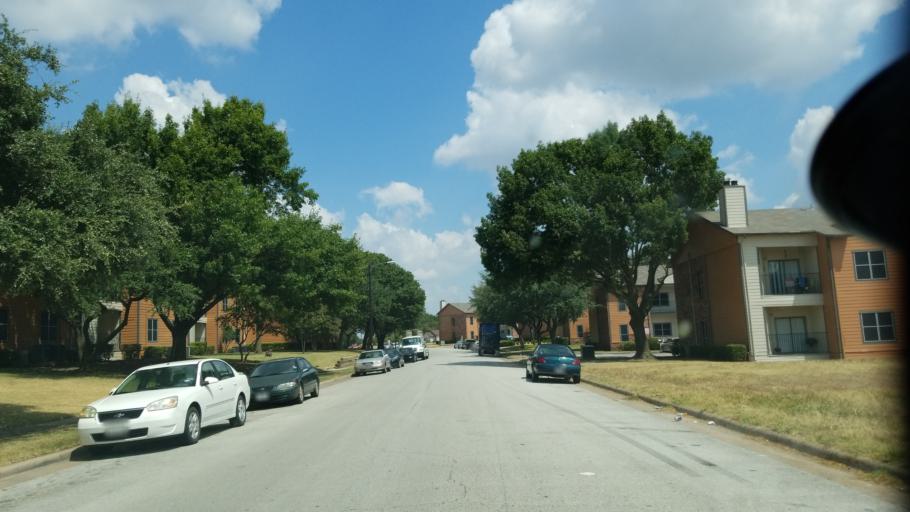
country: US
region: Texas
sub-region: Dallas County
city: Cockrell Hill
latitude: 32.6924
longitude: -96.8874
